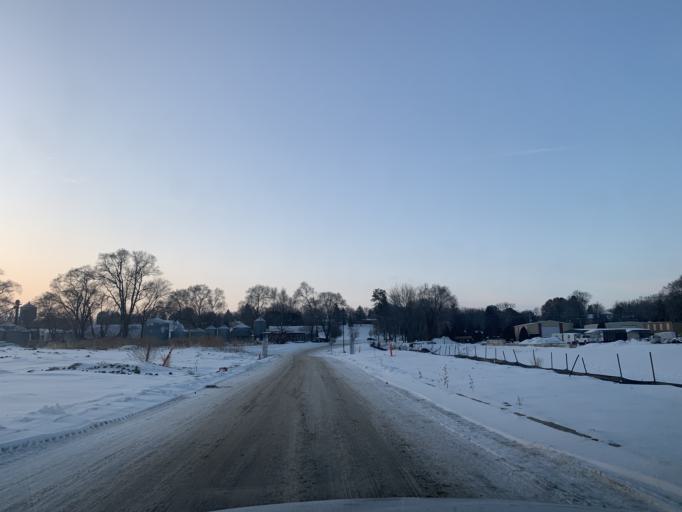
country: US
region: Minnesota
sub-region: Scott County
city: Shakopee
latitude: 44.7887
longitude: -93.4897
